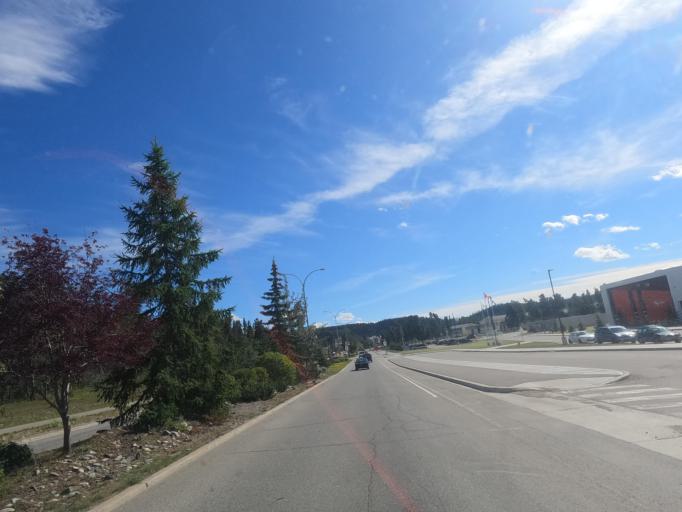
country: CA
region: Yukon
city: Whitehorse
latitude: 60.7110
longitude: -135.0389
